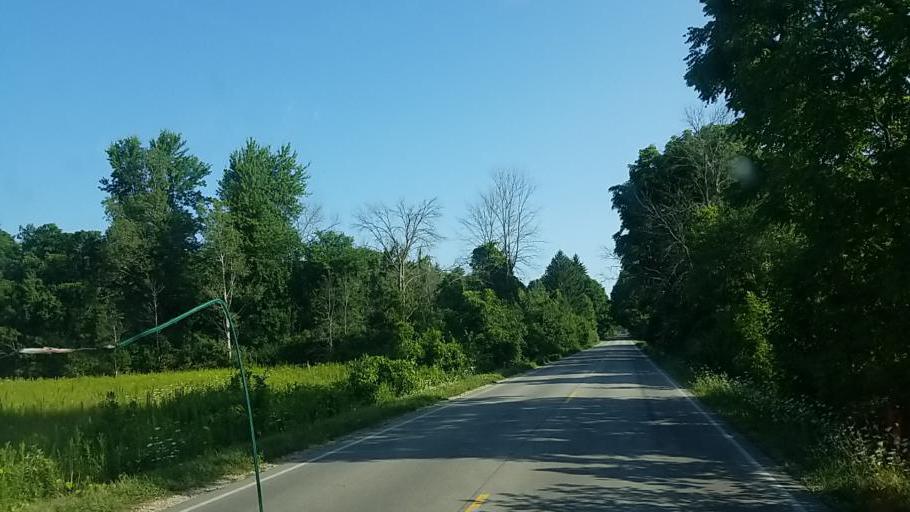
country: US
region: Michigan
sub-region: Newaygo County
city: Fremont
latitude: 43.3846
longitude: -85.9394
